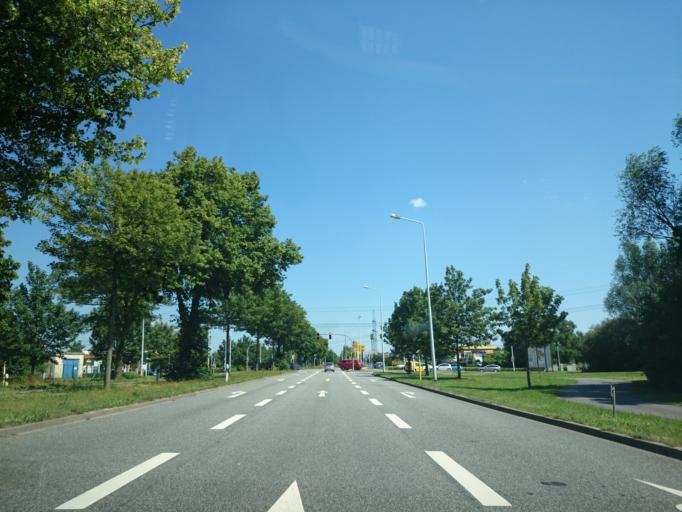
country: DE
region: Mecklenburg-Vorpommern
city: Roggentin
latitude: 54.0804
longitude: 12.2109
